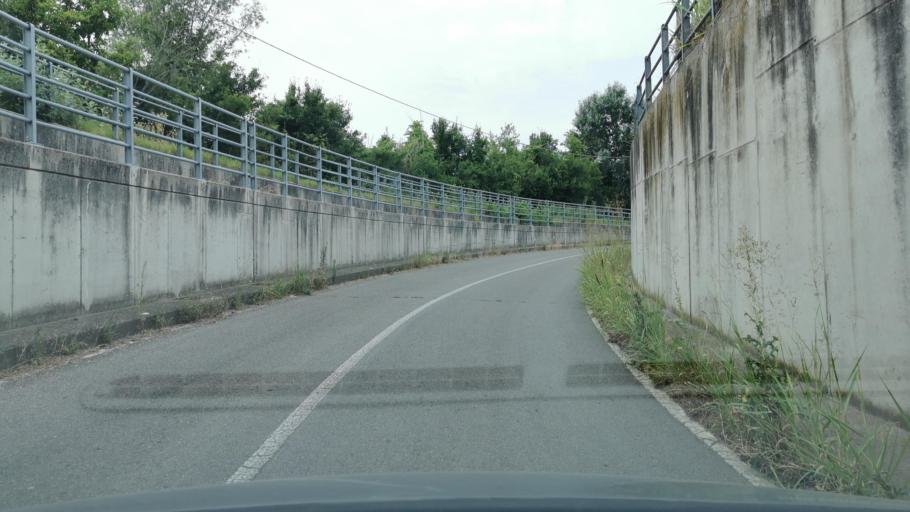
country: IT
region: Emilia-Romagna
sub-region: Provincia di Modena
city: Campogalliano
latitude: 44.6896
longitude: 10.8810
